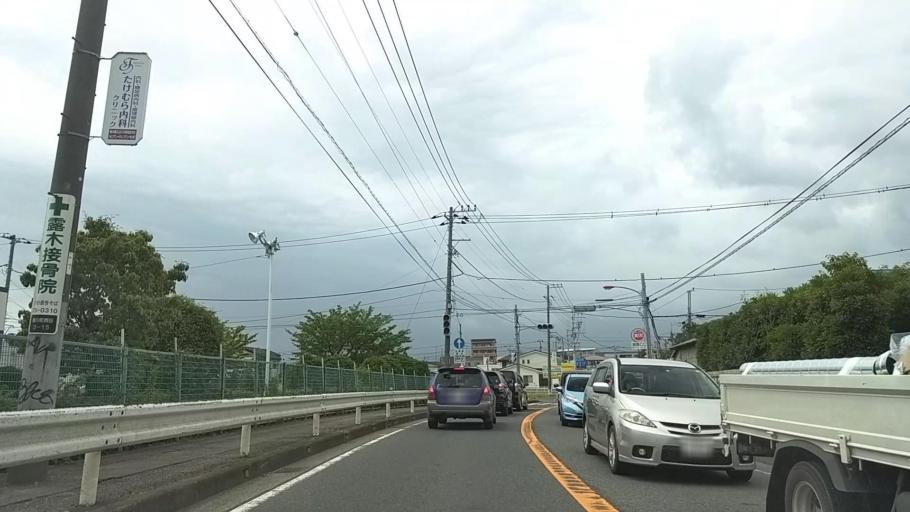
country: JP
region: Kanagawa
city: Chigasaki
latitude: 35.3675
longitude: 139.3916
